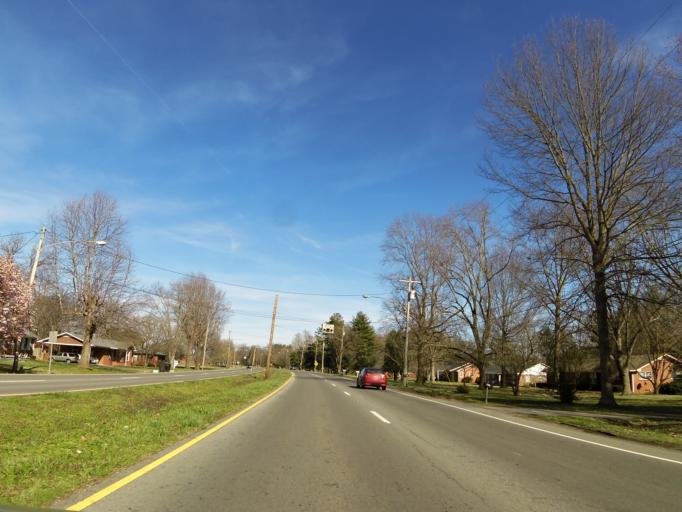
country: US
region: Tennessee
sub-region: Rutherford County
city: Murfreesboro
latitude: 35.8362
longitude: -86.3700
